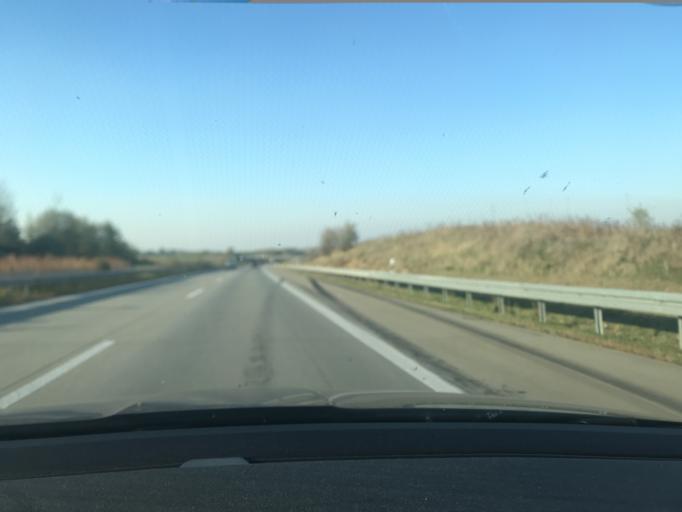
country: DE
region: Saxony
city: Liebstadt
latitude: 50.8576
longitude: 13.8753
